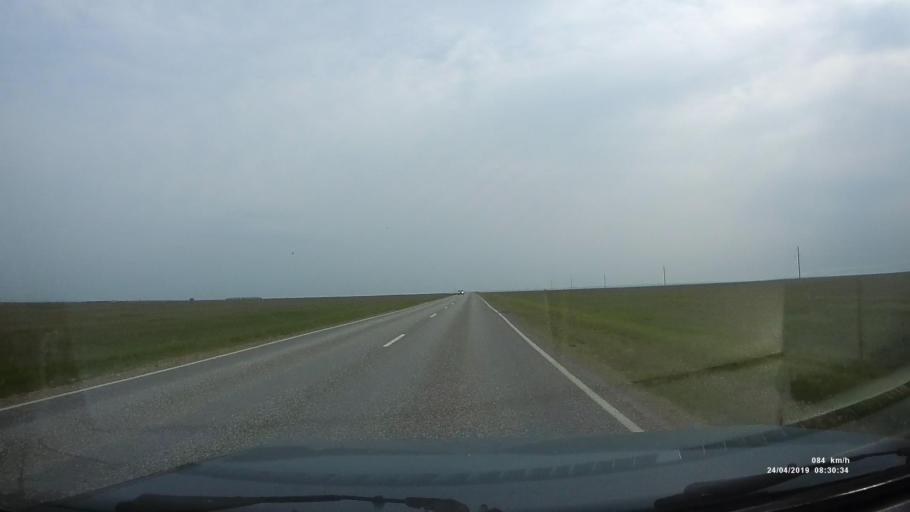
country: RU
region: Kalmykiya
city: Priyutnoye
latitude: 46.1605
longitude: 43.8475
